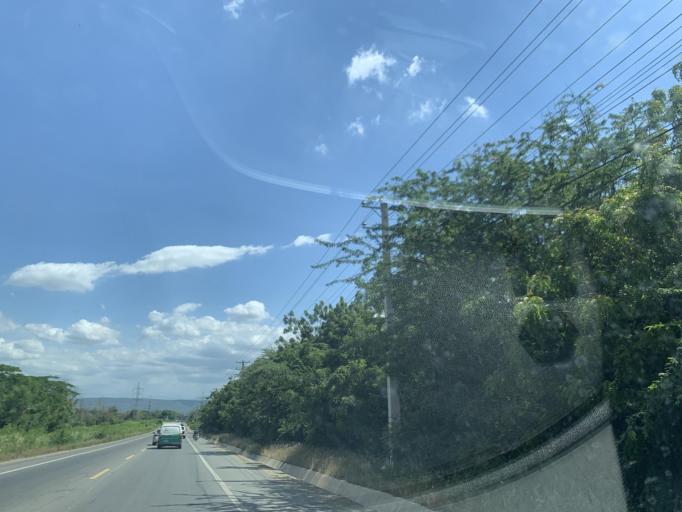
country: DO
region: Santiago
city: Villa Bisono
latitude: 19.5652
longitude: -70.8574
